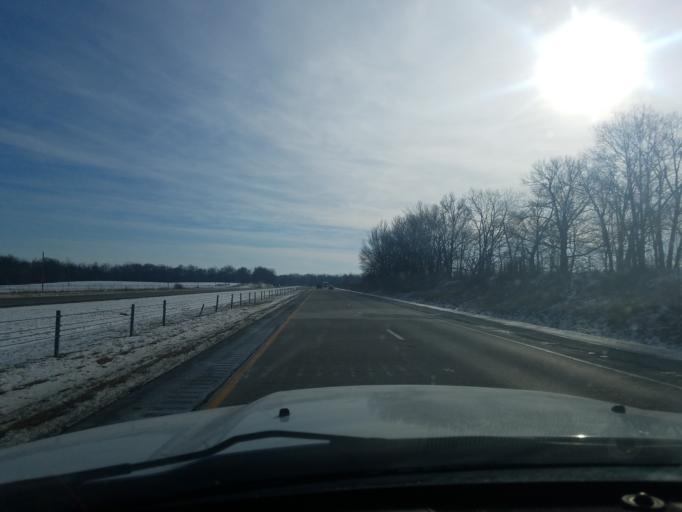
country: US
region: Indiana
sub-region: Grant County
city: Upland
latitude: 40.4662
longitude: -85.5508
